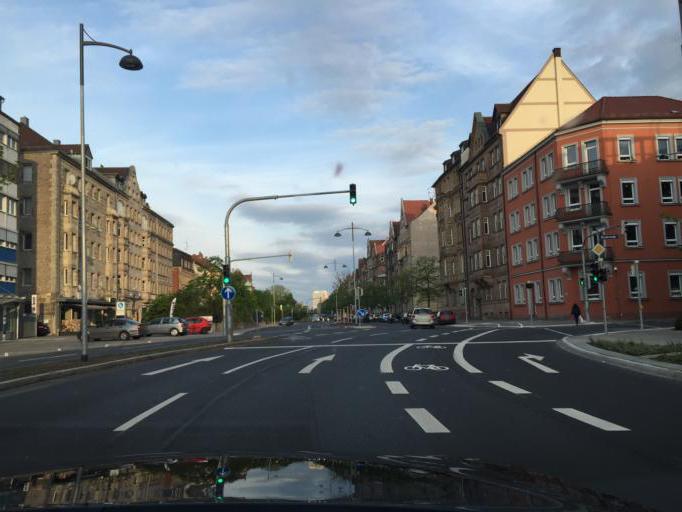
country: DE
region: Bavaria
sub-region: Regierungsbezirk Mittelfranken
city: Wetzendorf
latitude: 49.4535
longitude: 11.0476
